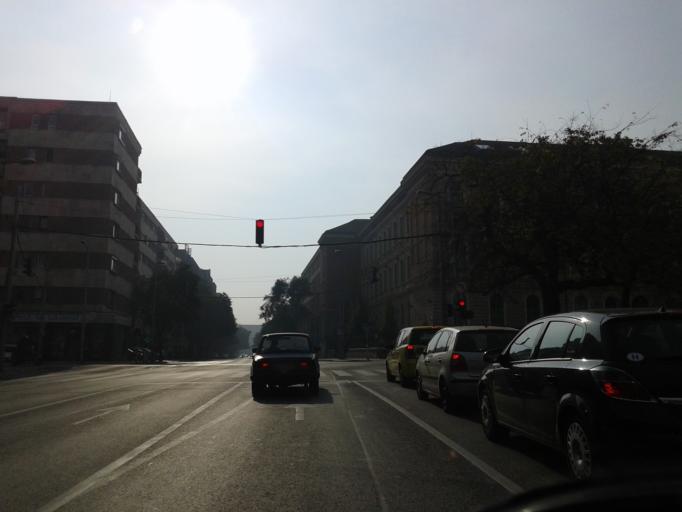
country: HU
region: Budapest
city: Budapest III. keruelet
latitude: 47.5278
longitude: 19.0385
